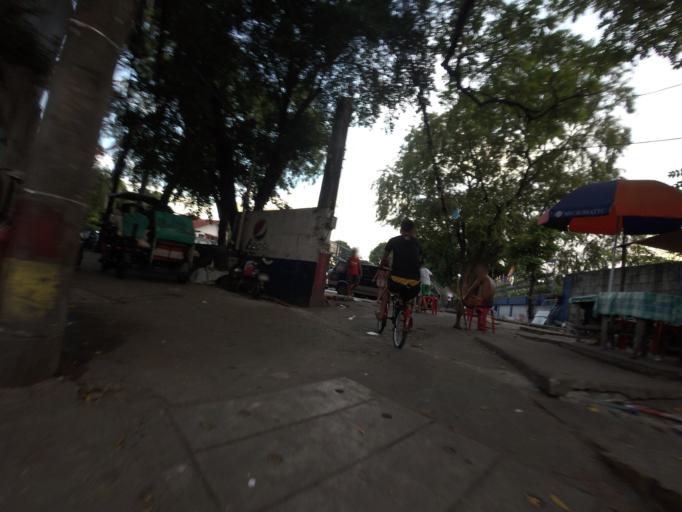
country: PH
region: Metro Manila
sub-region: City of Manila
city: Quiapo
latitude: 14.5926
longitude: 120.9913
